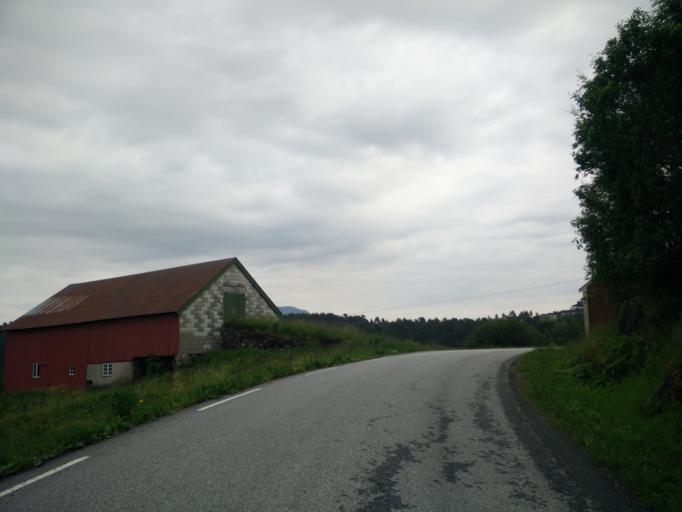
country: NO
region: More og Romsdal
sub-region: Kristiansund
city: Rensvik
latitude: 63.0194
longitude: 7.9621
